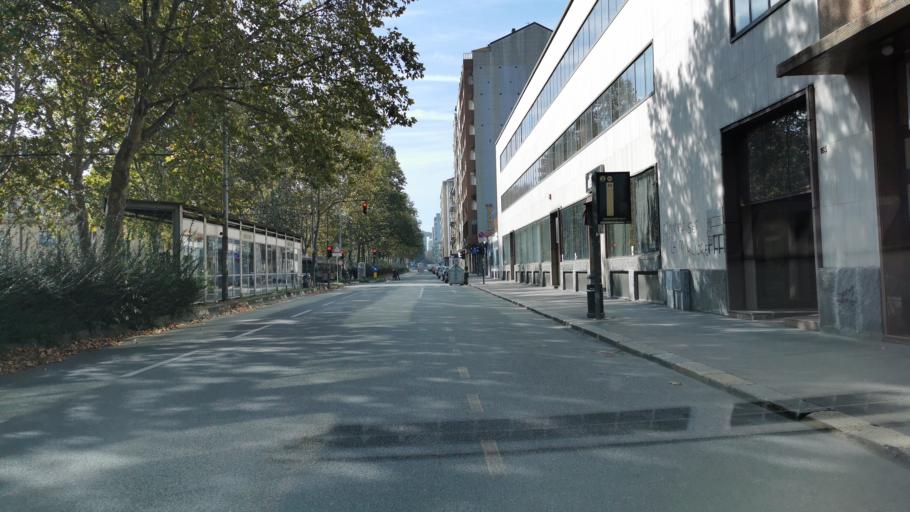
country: IT
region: Piedmont
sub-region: Provincia di Torino
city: Turin
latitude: 45.0896
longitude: 7.6596
